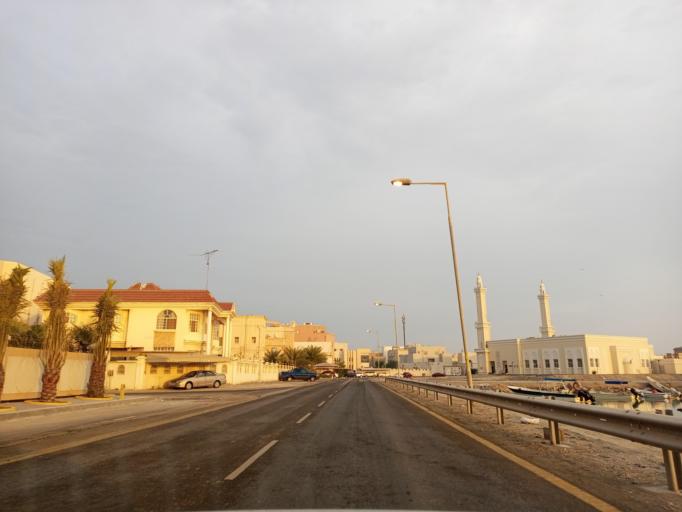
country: BH
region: Muharraq
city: Al Hadd
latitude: 26.2453
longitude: 50.6460
